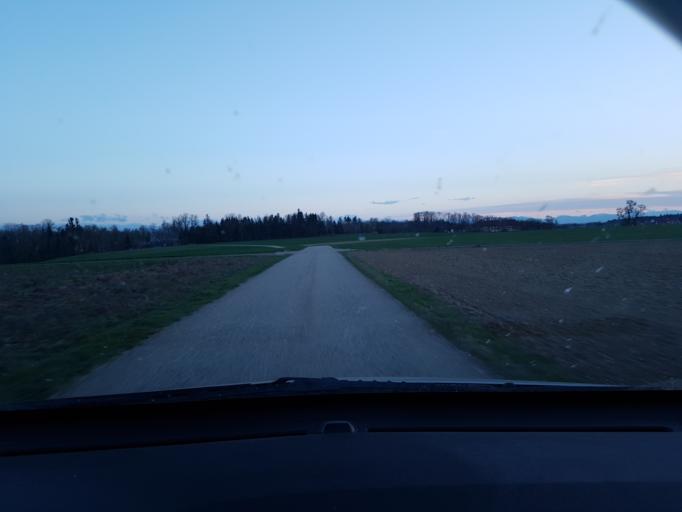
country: AT
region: Upper Austria
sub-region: Politischer Bezirk Linz-Land
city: Ansfelden
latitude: 48.1700
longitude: 14.3210
